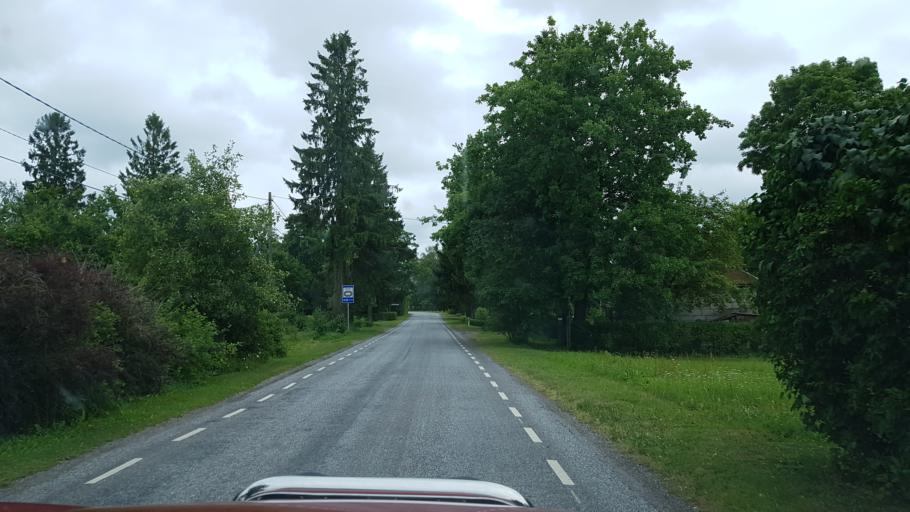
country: EE
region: Ida-Virumaa
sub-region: Puessi linn
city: Pussi
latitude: 59.3822
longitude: 27.0358
